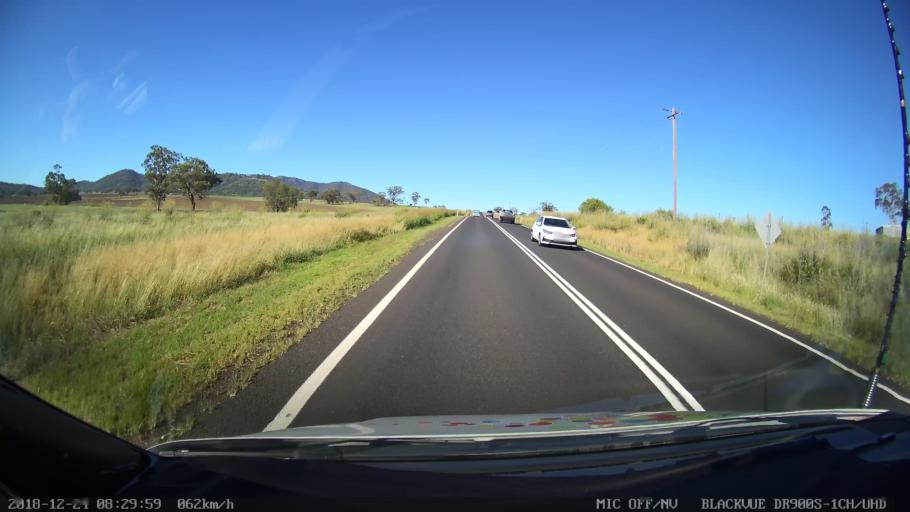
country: AU
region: New South Wales
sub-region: Tamworth Municipality
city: Phillip
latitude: -31.2655
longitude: 150.7293
